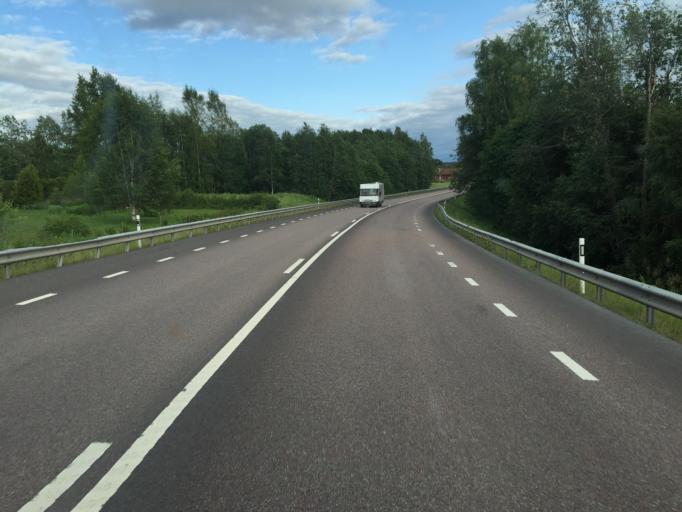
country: SE
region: Dalarna
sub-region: Gagnefs Kommun
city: Djuras
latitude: 60.5794
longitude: 15.1185
